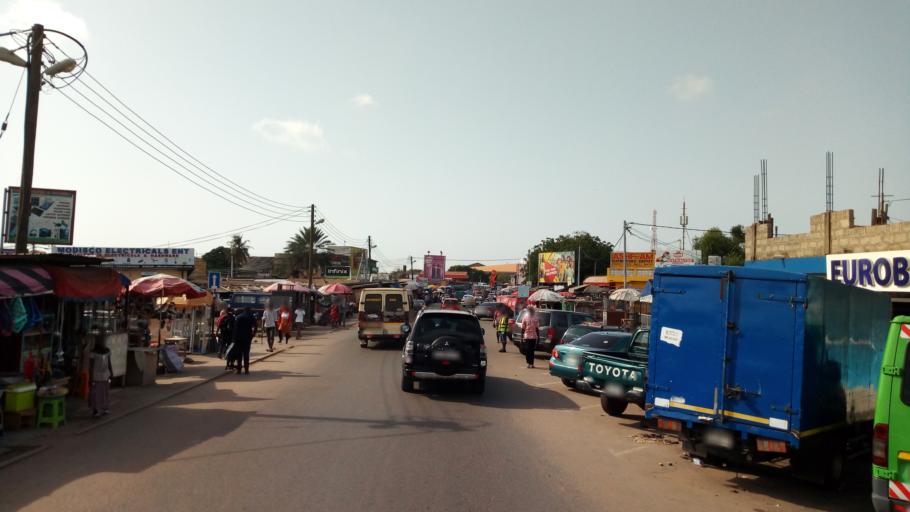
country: GH
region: Greater Accra
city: Tema
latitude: 5.6457
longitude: -0.0011
